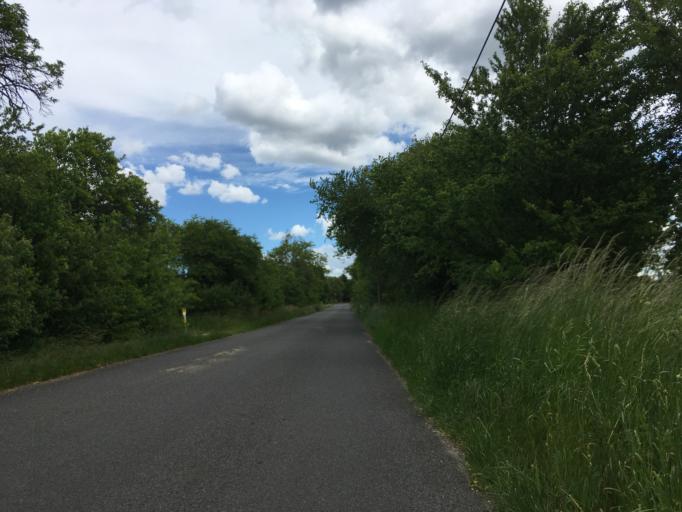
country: DE
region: Brandenburg
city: Falkenberg
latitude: 52.7728
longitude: 13.9442
